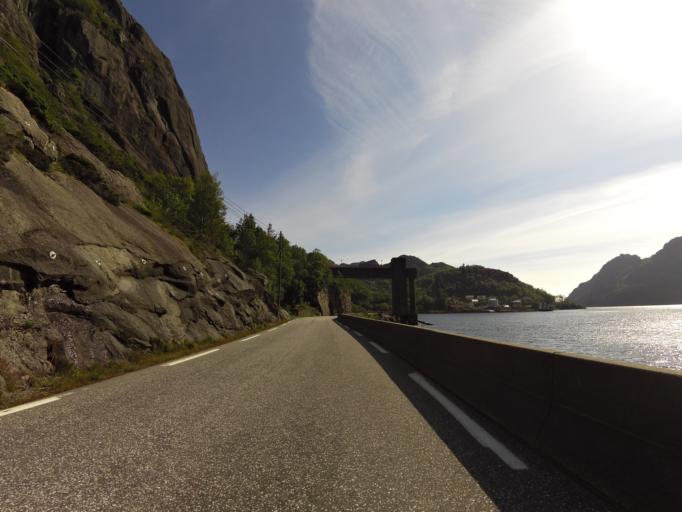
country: NO
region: Rogaland
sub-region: Sokndal
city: Hauge i Dalane
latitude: 58.3212
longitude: 6.3495
